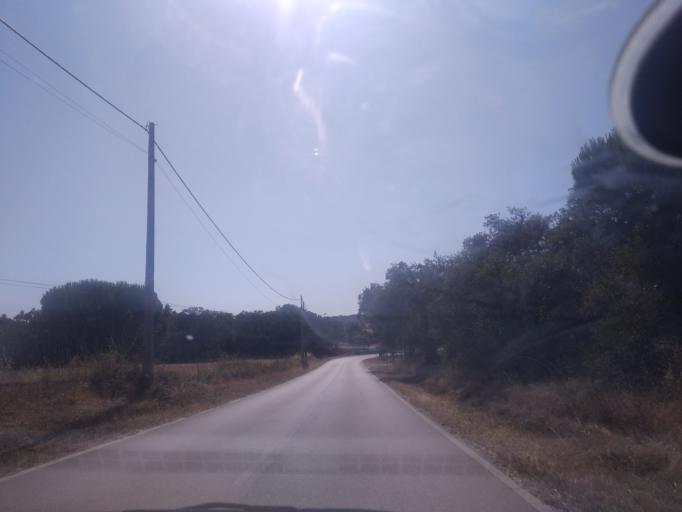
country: PT
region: Faro
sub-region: Aljezur
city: Aljezur
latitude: 37.2275
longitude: -8.8222
